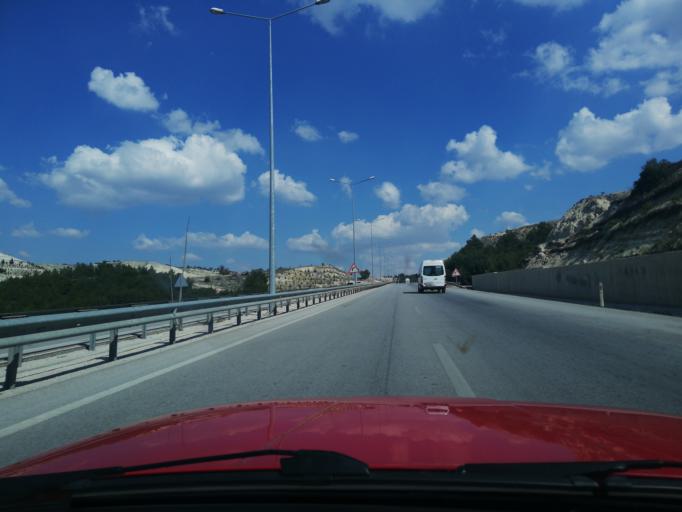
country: TR
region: Burdur
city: Burdur
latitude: 37.7011
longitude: 30.3117
